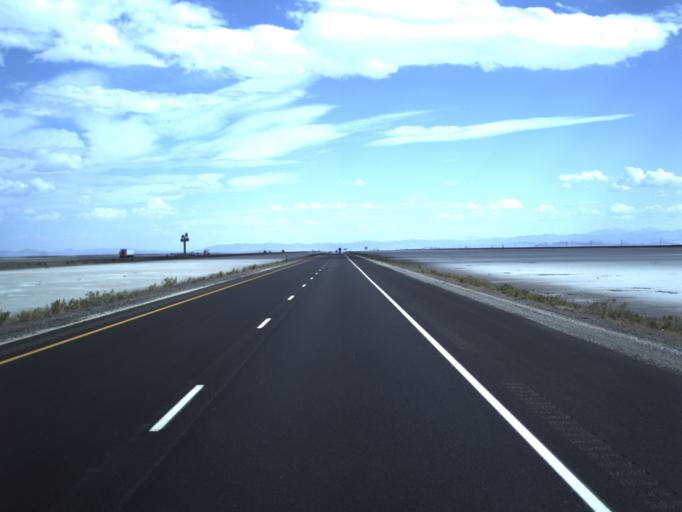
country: US
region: Utah
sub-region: Tooele County
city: Wendover
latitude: 40.7323
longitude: -113.5633
